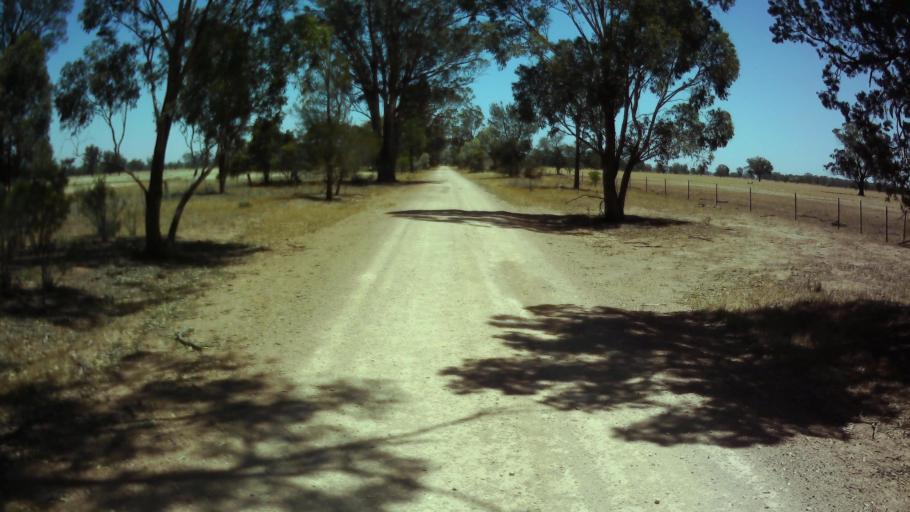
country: AU
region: New South Wales
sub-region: Weddin
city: Grenfell
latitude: -33.9900
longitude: 147.9391
